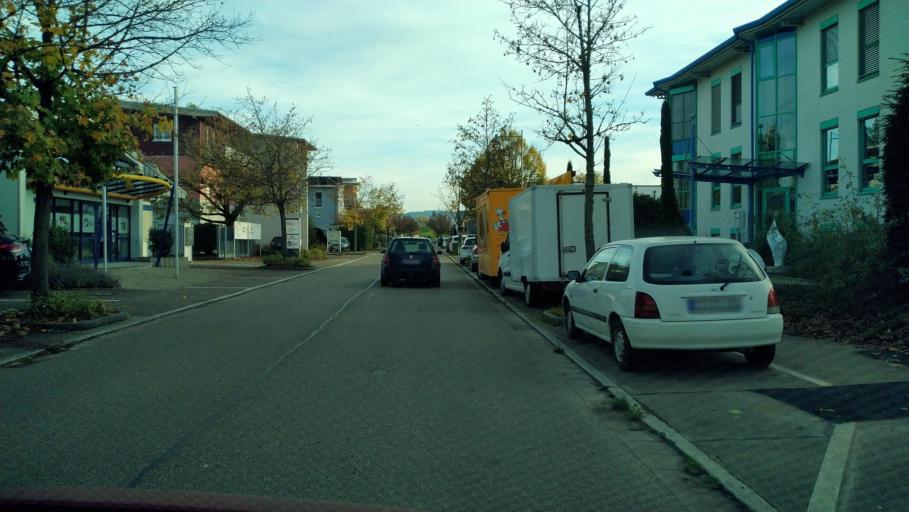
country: DE
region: Baden-Wuerttemberg
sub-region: Freiburg Region
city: Emmendingen
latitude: 48.1129
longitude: 7.8470
